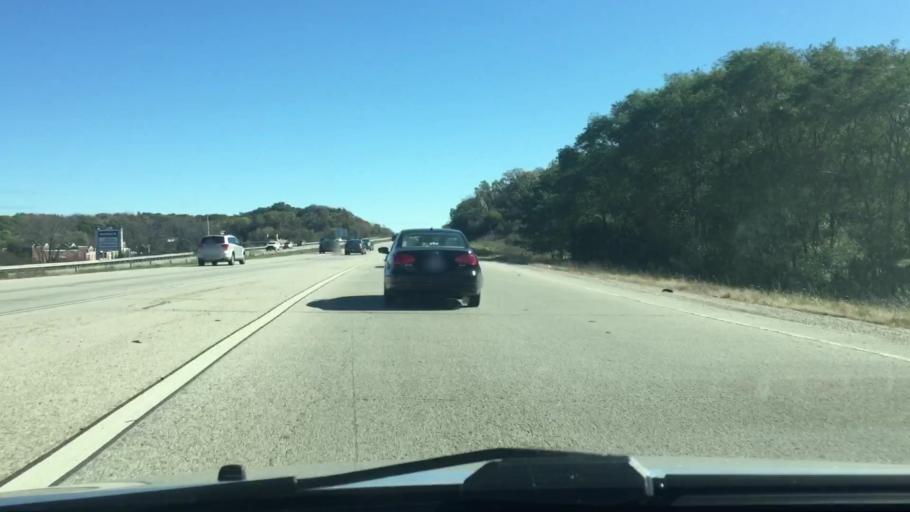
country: US
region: Wisconsin
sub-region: Waukesha County
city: Delafield
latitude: 43.0518
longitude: -88.3685
